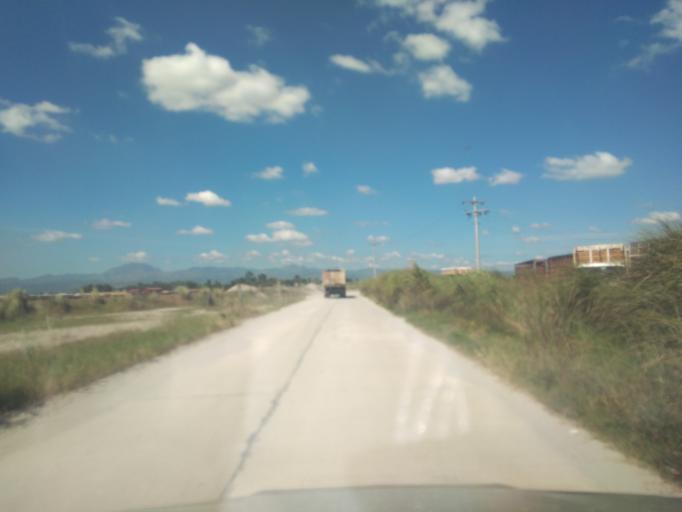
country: PH
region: Central Luzon
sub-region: Province of Pampanga
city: Balas
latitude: 15.0592
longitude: 120.5962
